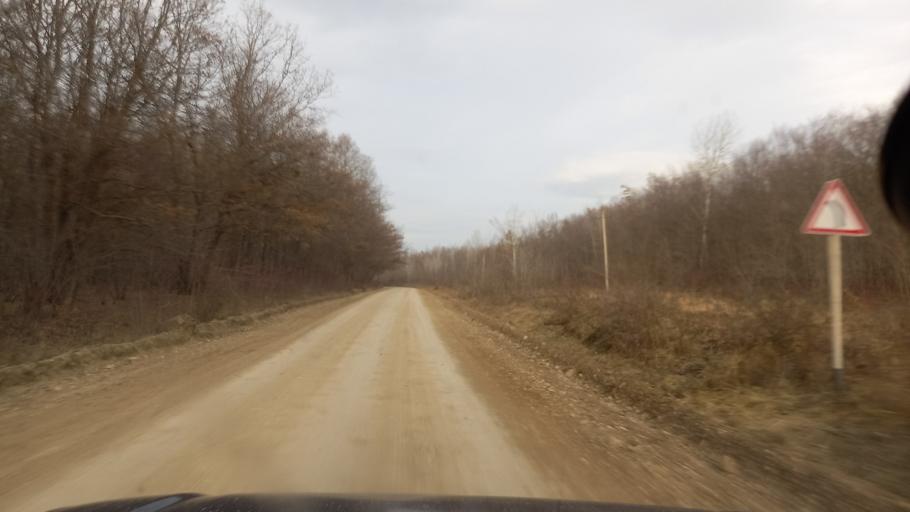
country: RU
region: Adygeya
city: Kamennomostskiy
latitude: 44.1778
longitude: 40.2562
